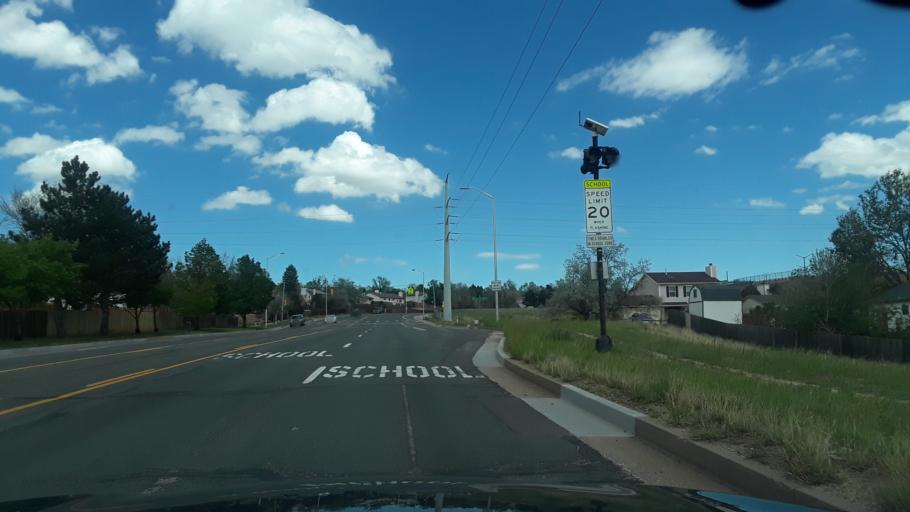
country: US
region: Colorado
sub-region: El Paso County
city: Air Force Academy
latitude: 38.9442
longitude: -104.7860
